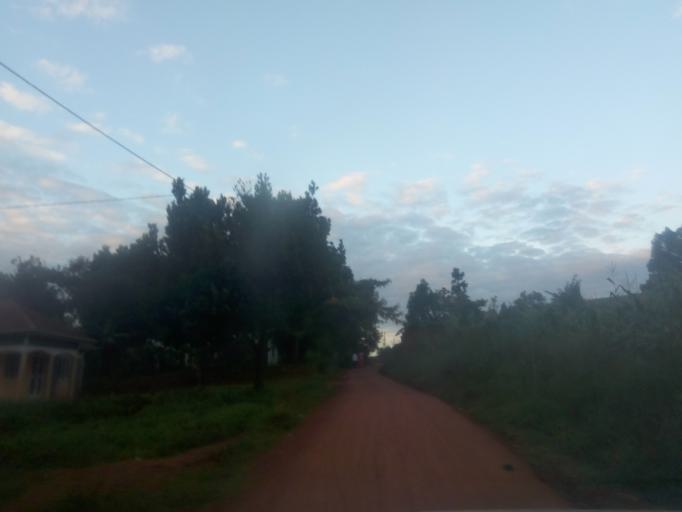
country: UG
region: Central Region
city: Kampala Central Division
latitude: 0.3893
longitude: 32.5639
